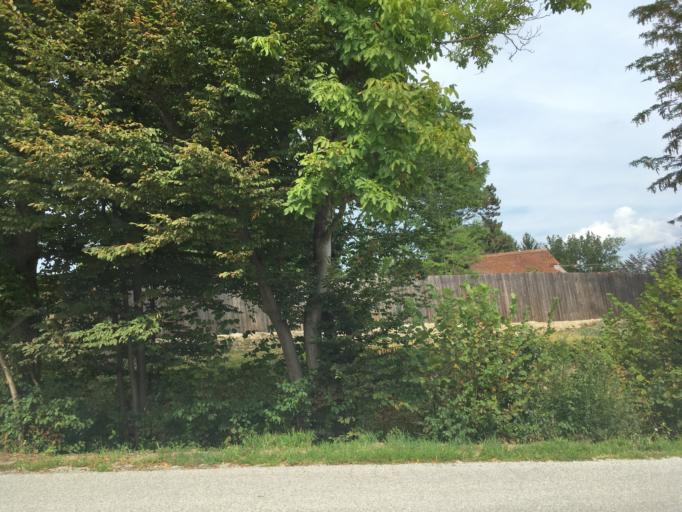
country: AT
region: Styria
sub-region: Politischer Bezirk Hartberg-Fuerstenfeld
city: Hartberg
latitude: 47.2794
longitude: 15.9651
